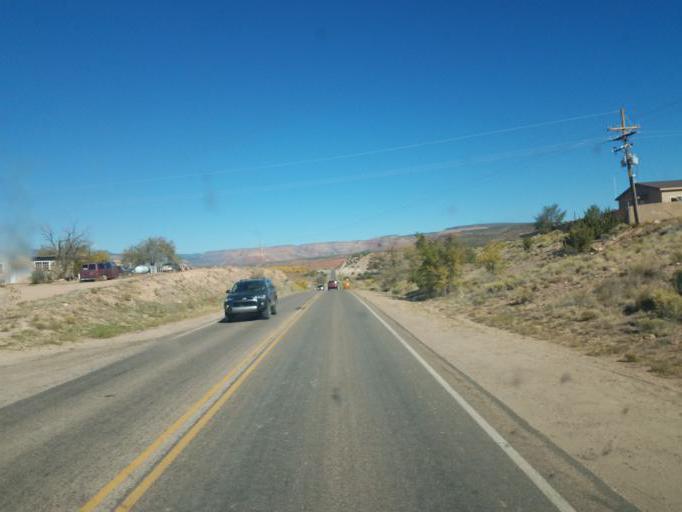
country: US
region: New Mexico
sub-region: Sandoval County
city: Jemez Pueblo
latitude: 35.6203
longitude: -106.7238
